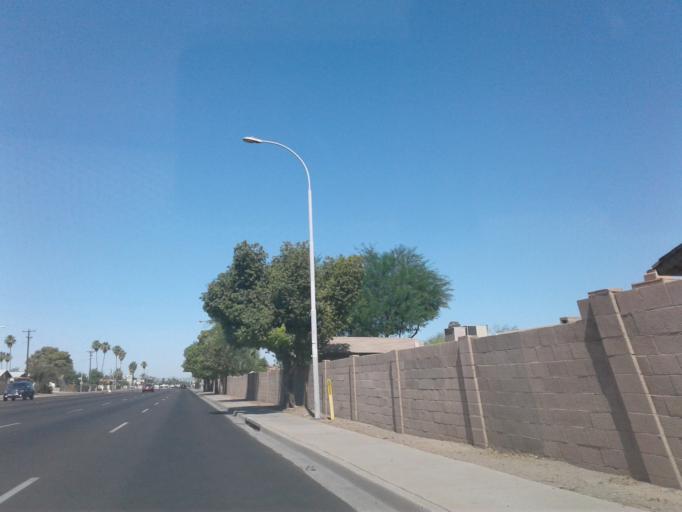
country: US
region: Arizona
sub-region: Maricopa County
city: Tolleson
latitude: 33.4945
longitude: -112.2318
